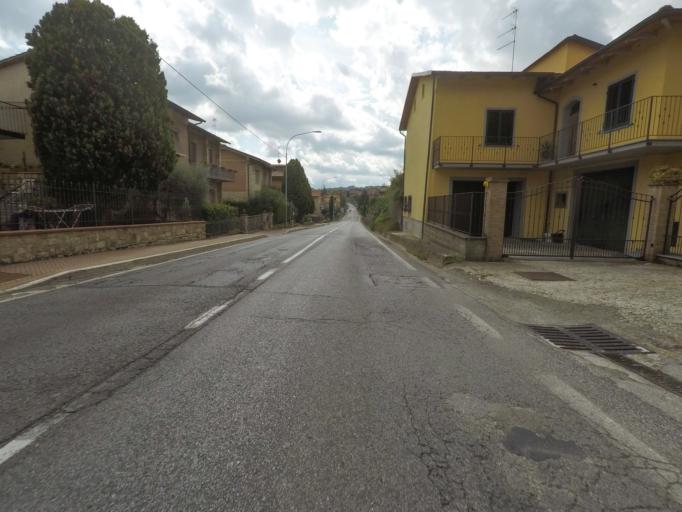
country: IT
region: Tuscany
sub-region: Provincia di Siena
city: Torrita di Siena
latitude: 43.1727
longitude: 11.7740
